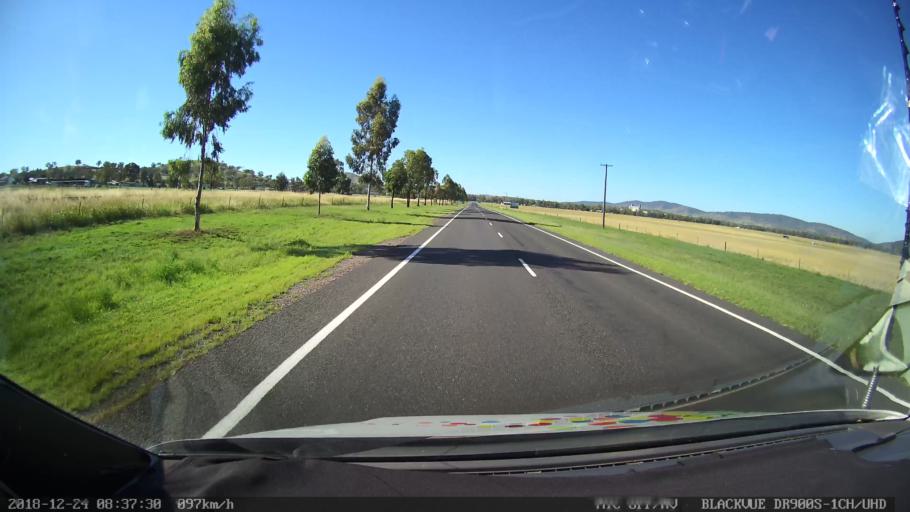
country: AU
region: New South Wales
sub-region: Liverpool Plains
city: Quirindi
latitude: -31.3298
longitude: 150.6487
